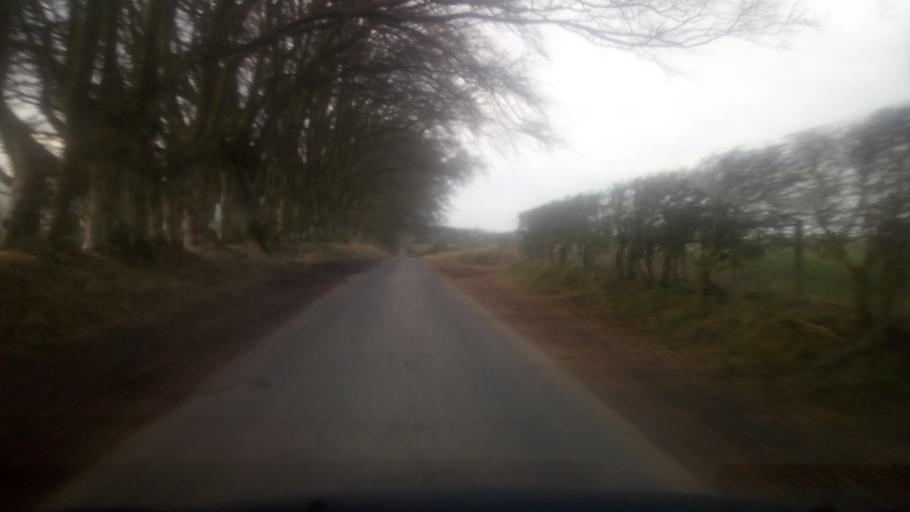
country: GB
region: Scotland
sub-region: The Scottish Borders
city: Jedburgh
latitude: 55.4113
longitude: -2.6127
